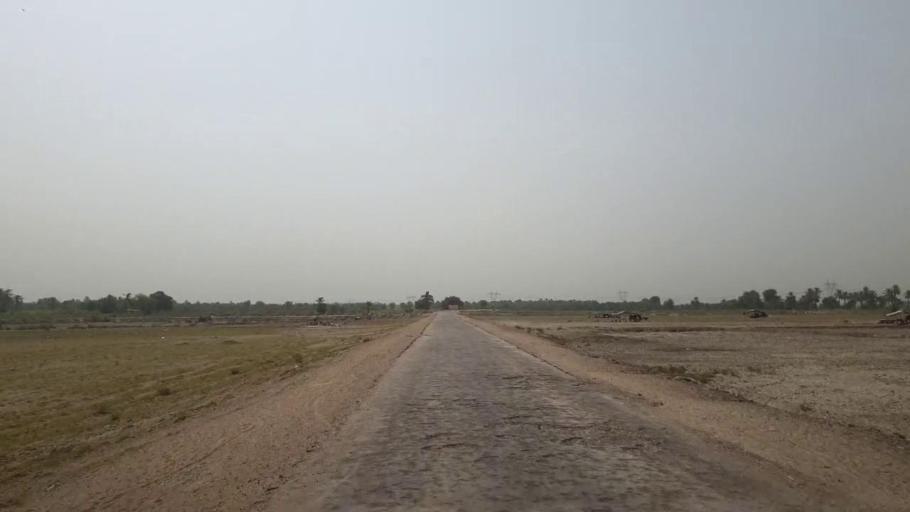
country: PK
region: Sindh
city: Gambat
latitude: 27.4224
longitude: 68.5447
